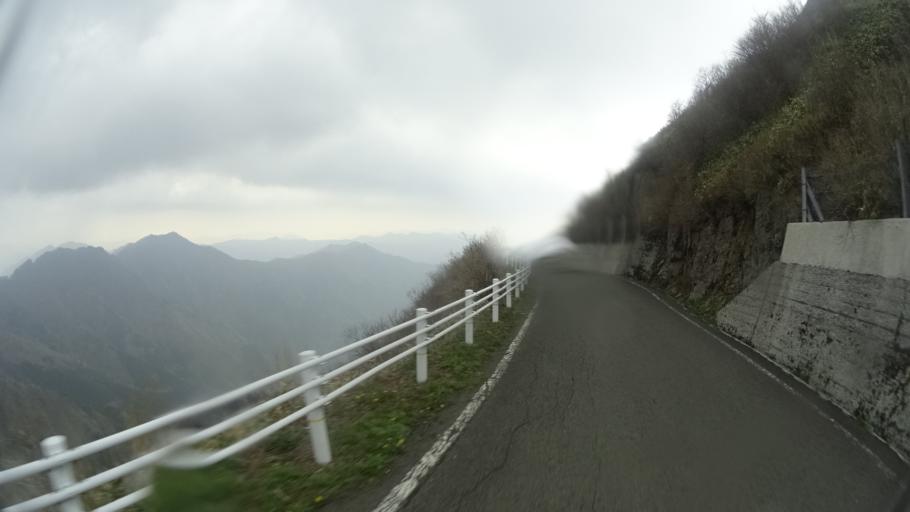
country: JP
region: Ehime
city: Saijo
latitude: 33.7810
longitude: 133.2245
